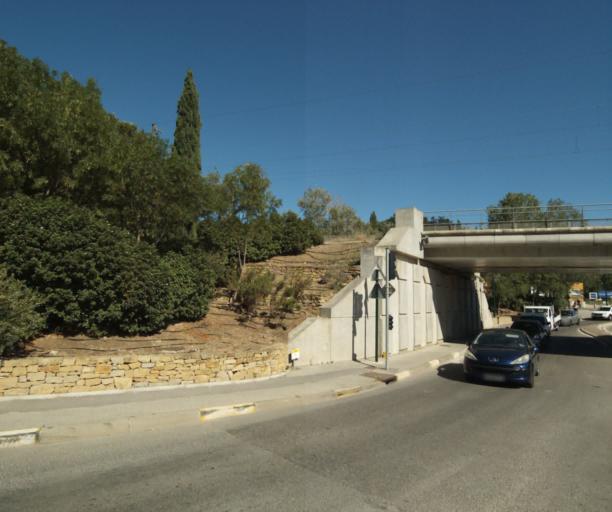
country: FR
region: Provence-Alpes-Cote d'Azur
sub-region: Departement du Var
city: La Garde
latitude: 43.1196
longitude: 6.0110
